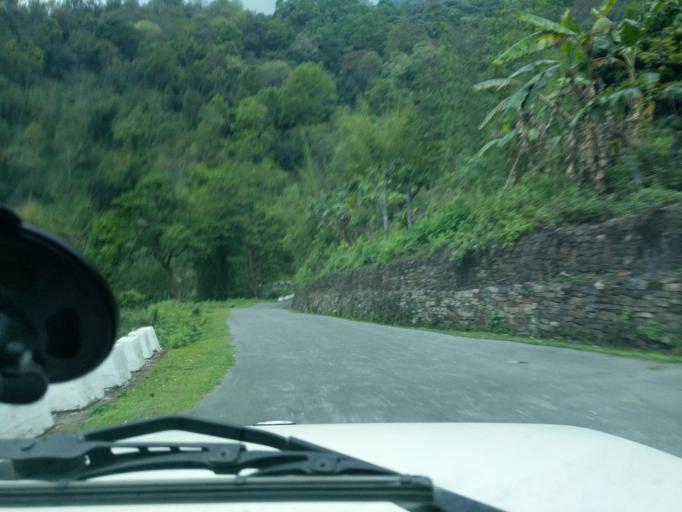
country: BT
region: Mongar
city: Mongar
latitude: 27.3021
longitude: 91.1521
